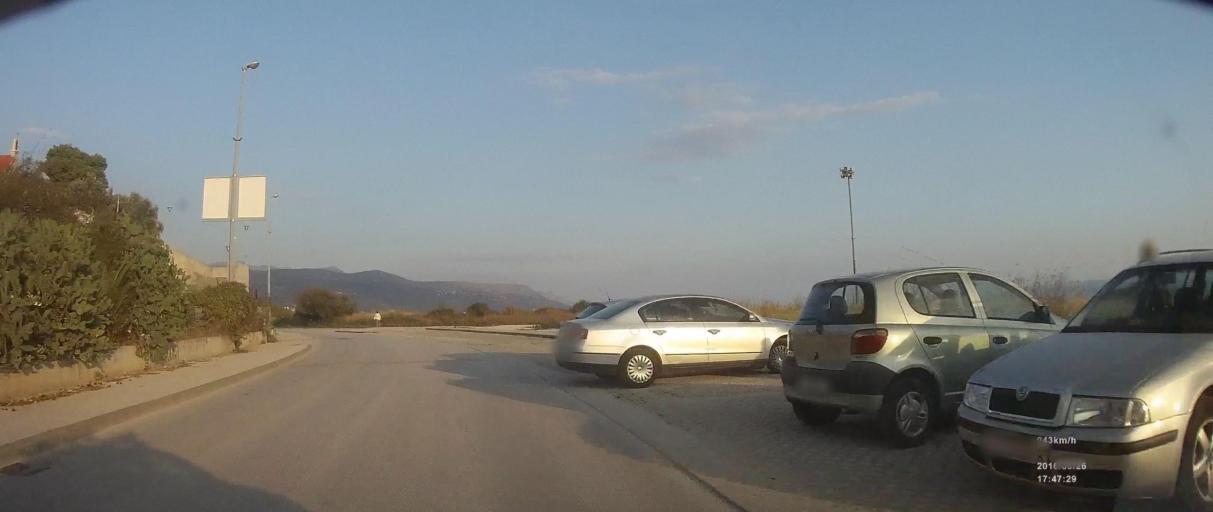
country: HR
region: Splitsko-Dalmatinska
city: Kamen
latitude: 43.5019
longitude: 16.4825
